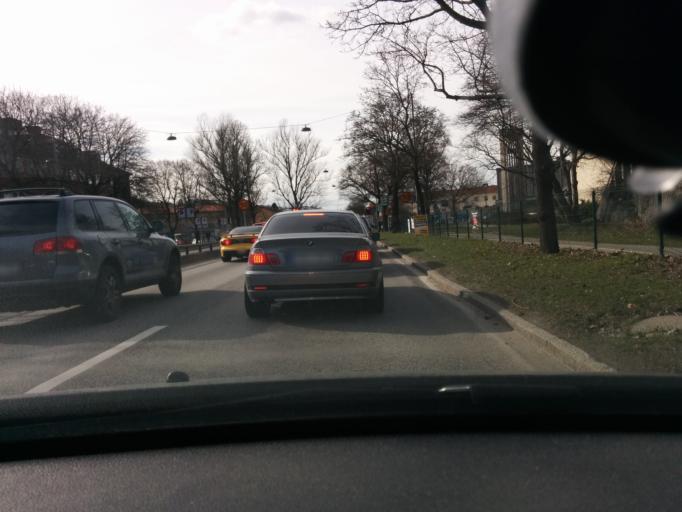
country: SE
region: Stockholm
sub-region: Stockholms Kommun
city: Bromma
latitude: 59.3394
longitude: 17.9419
